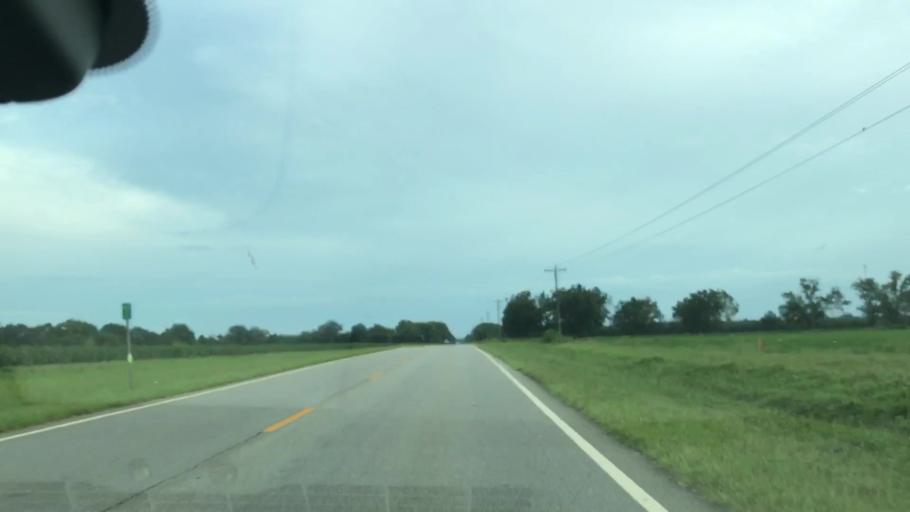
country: US
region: Georgia
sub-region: Quitman County
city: Georgetown
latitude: 31.8079
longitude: -85.0933
